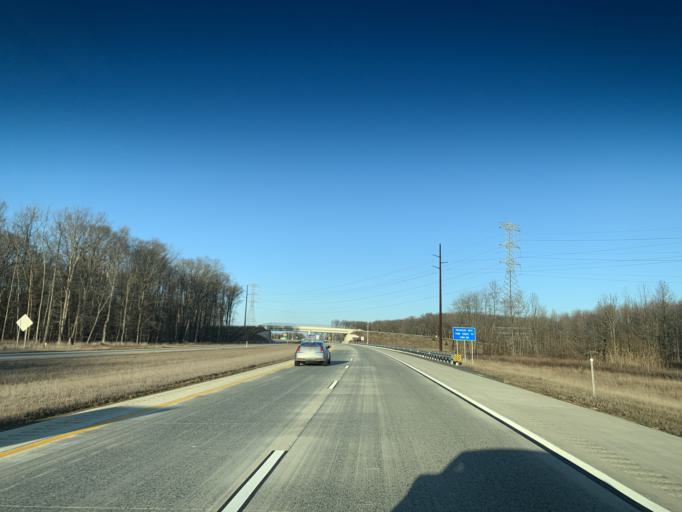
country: US
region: Delaware
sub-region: New Castle County
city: Middletown
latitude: 39.4129
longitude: -75.7684
